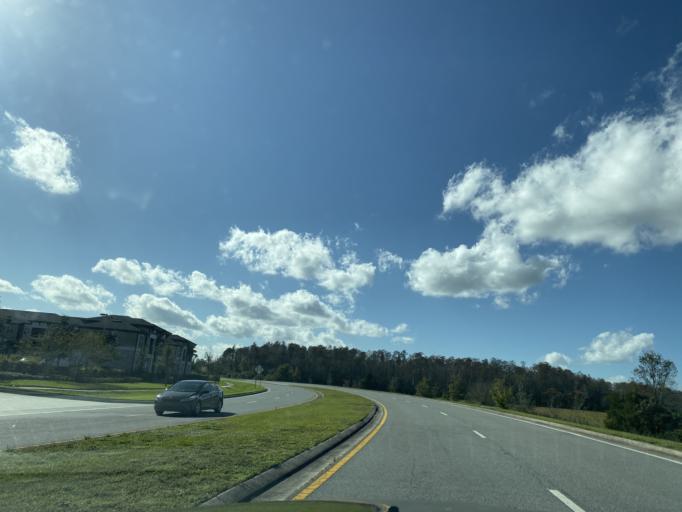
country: US
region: Florida
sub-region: Orange County
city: Conway
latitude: 28.4323
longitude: -81.2588
